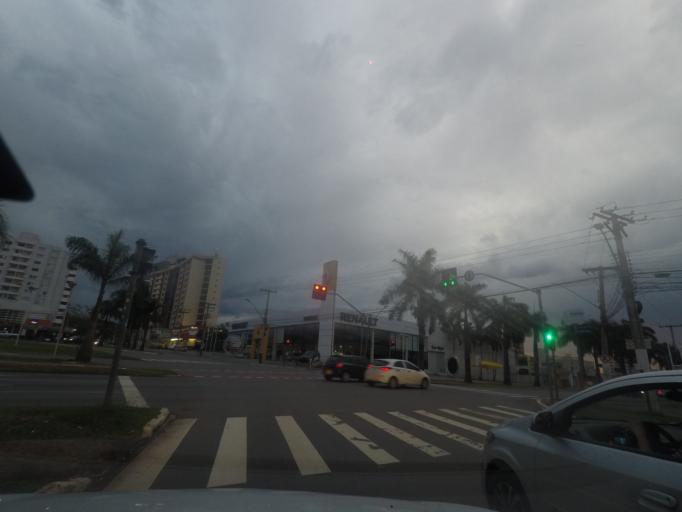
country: BR
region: Goias
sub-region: Goiania
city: Goiania
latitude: -16.7141
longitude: -49.2745
